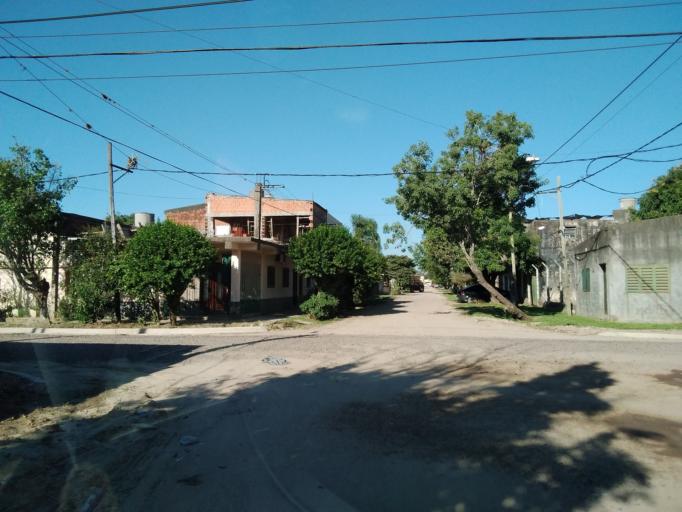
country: AR
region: Corrientes
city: Corrientes
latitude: -27.4806
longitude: -58.8138
